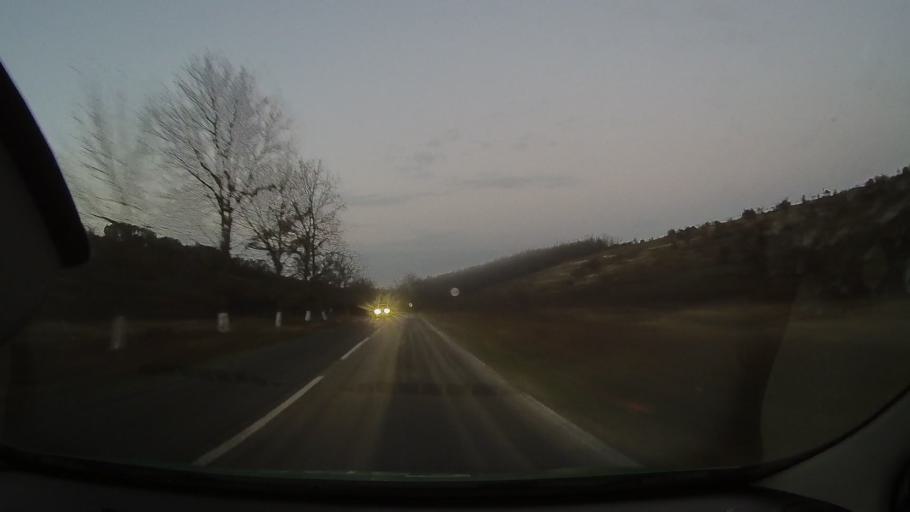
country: RO
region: Constanta
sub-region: Comuna Baneasa
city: Baneasa
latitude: 44.0761
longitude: 27.7378
